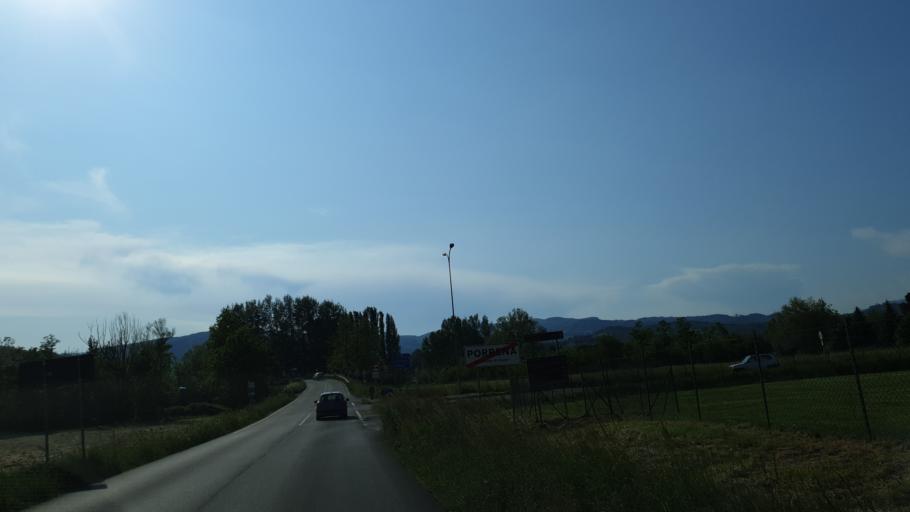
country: IT
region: Tuscany
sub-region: Province of Arezzo
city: Ponte a Poppi
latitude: 43.7401
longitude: 11.7427
